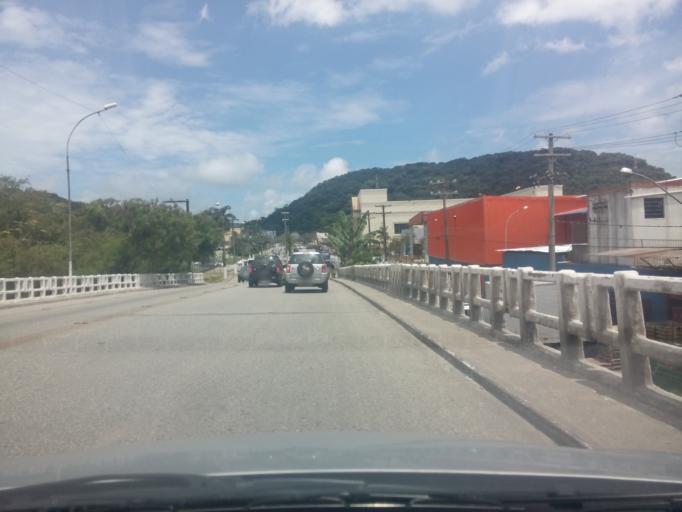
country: BR
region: Sao Paulo
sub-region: Guaruja
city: Guaruja
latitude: -23.9828
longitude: -46.2684
